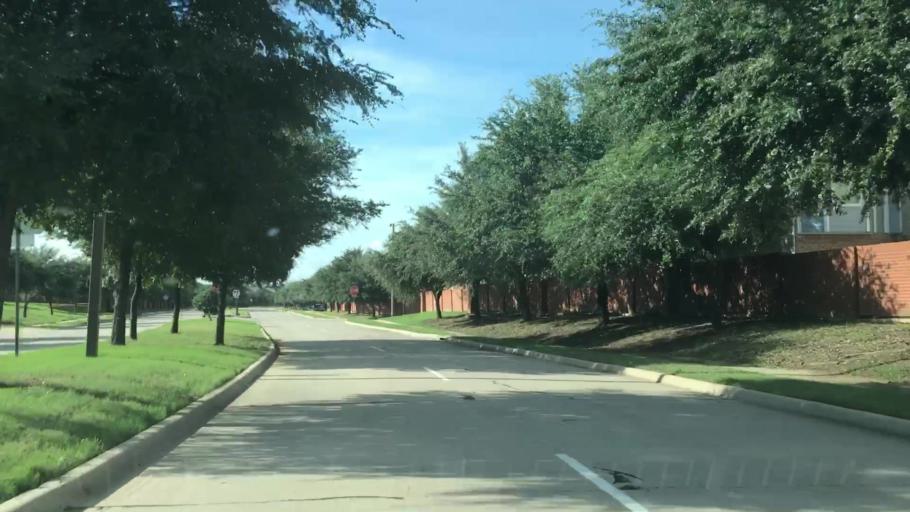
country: US
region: Texas
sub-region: Dallas County
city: Coppell
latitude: 32.9290
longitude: -96.9585
